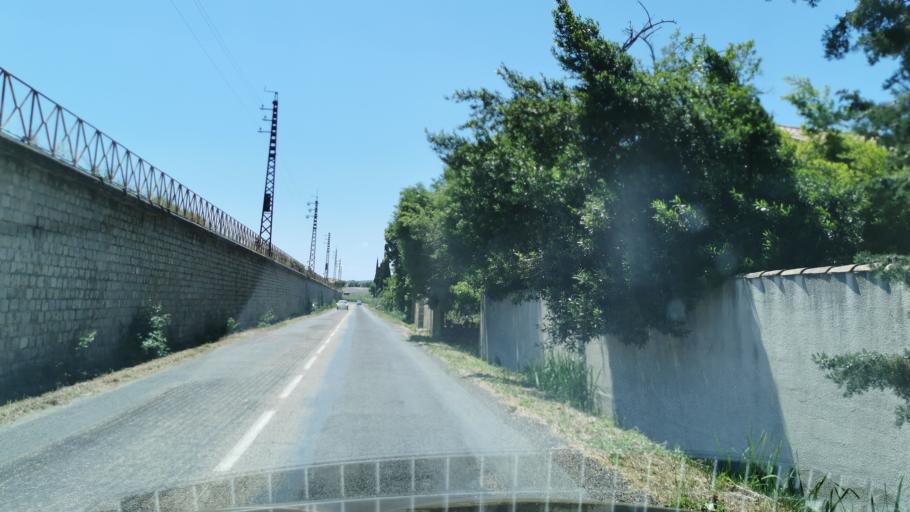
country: FR
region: Languedoc-Roussillon
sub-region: Departement de l'Aude
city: Narbonne
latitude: 43.1925
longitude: 3.0046
